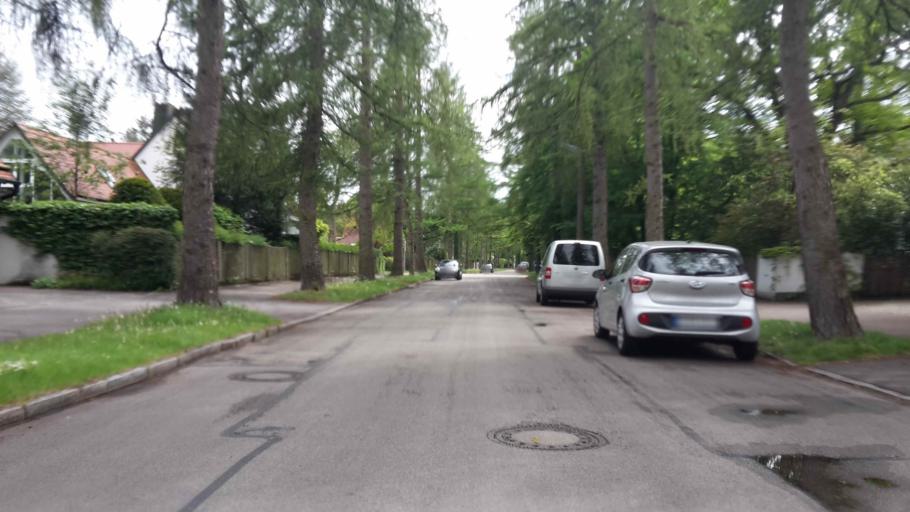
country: DE
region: Bavaria
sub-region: Upper Bavaria
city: Pasing
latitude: 48.1751
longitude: 11.4834
